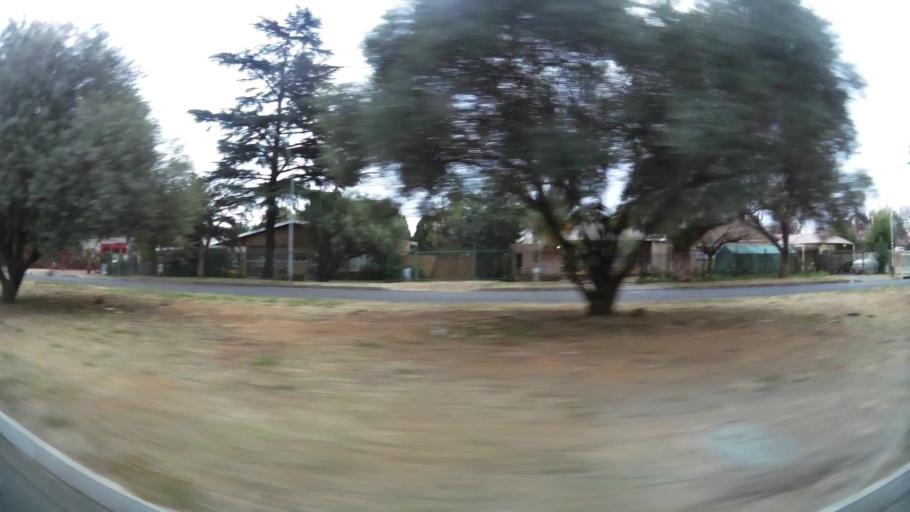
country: ZA
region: Orange Free State
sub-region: Mangaung Metropolitan Municipality
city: Bloemfontein
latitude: -29.1263
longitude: 26.1764
